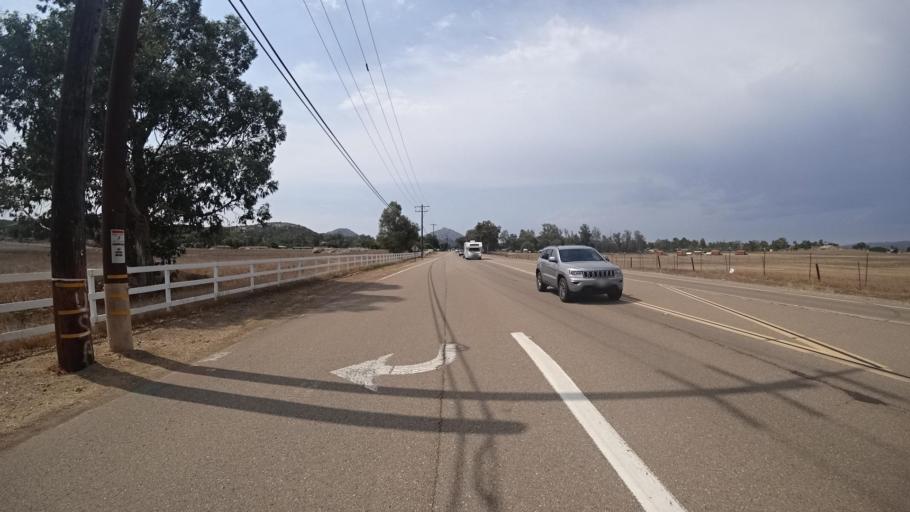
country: US
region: California
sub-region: San Diego County
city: Ramona
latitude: 33.0084
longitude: -116.8953
